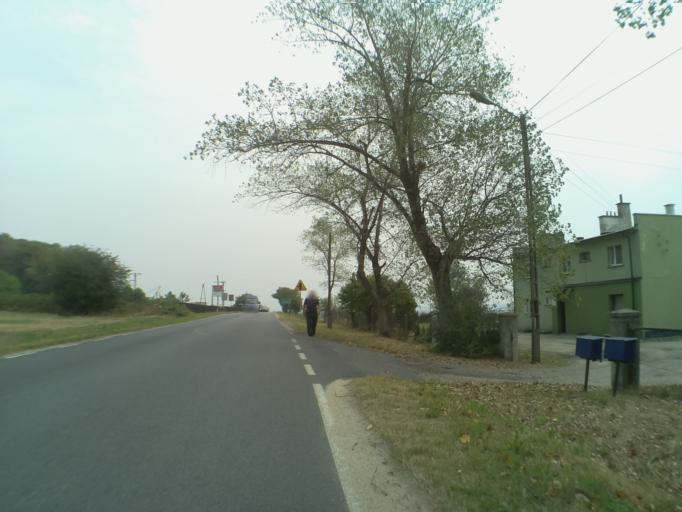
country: PL
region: Lower Silesian Voivodeship
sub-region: Powiat swidnicki
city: Strzegom
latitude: 50.9676
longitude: 16.3273
